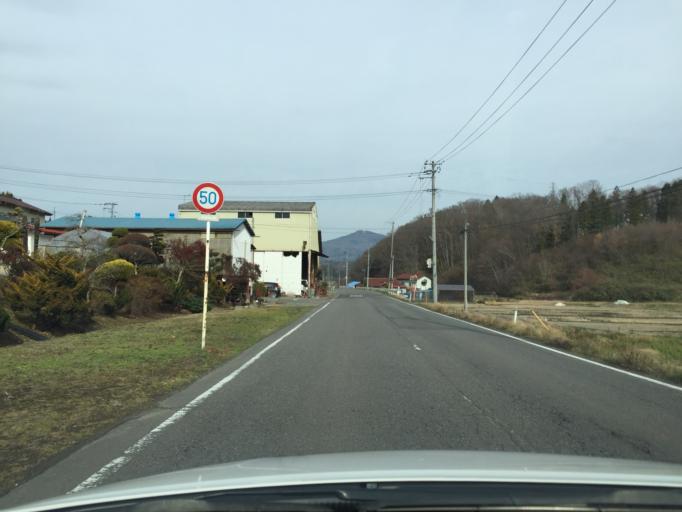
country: JP
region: Fukushima
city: Funehikimachi-funehiki
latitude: 37.4221
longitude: 140.5848
